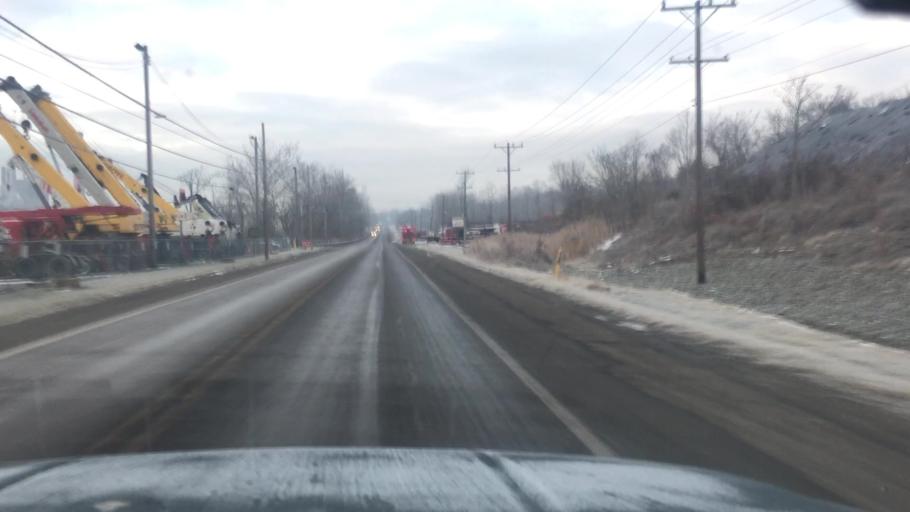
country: US
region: Pennsylvania
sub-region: Allegheny County
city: Elizabeth
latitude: 40.2621
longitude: -79.9111
